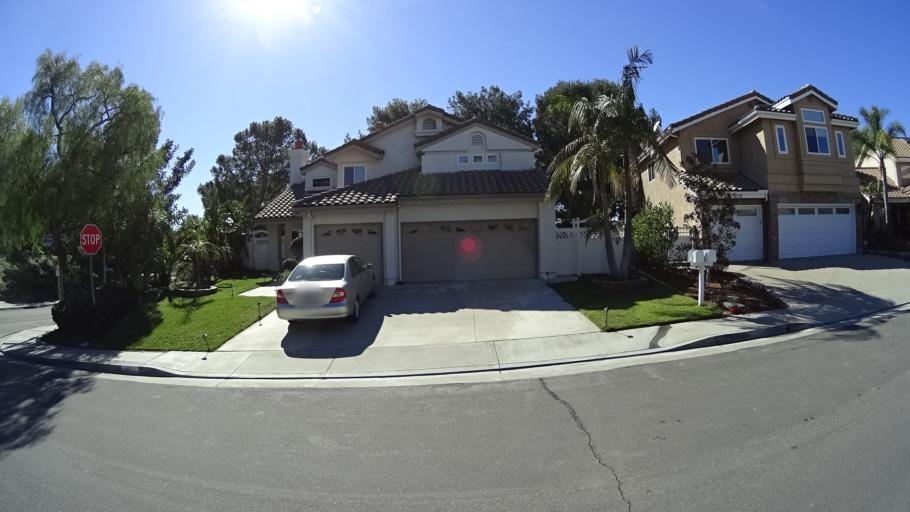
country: US
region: California
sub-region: Orange County
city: Villa Park
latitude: 33.8455
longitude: -117.7434
